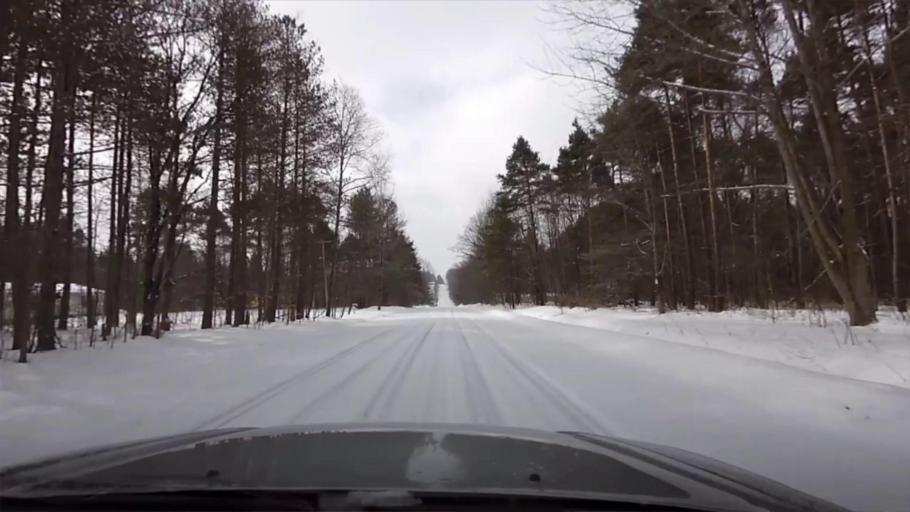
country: US
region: New York
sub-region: Cattaraugus County
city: Franklinville
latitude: 42.3247
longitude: -78.3540
